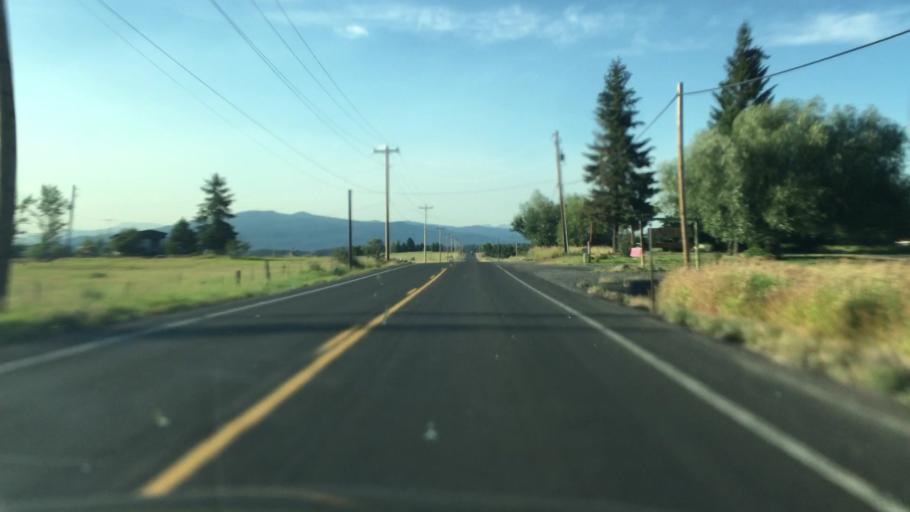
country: US
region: Idaho
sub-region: Valley County
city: McCall
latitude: 44.8711
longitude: -116.0908
